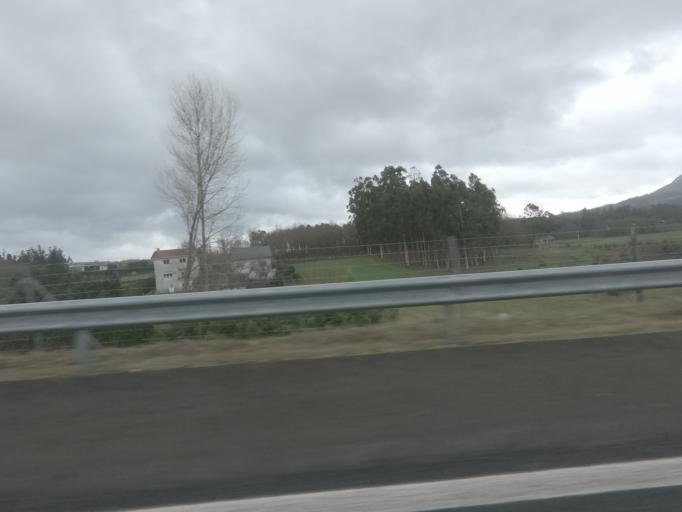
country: ES
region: Galicia
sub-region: Provincia da Coruna
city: Vedra
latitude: 42.8171
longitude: -8.4873
